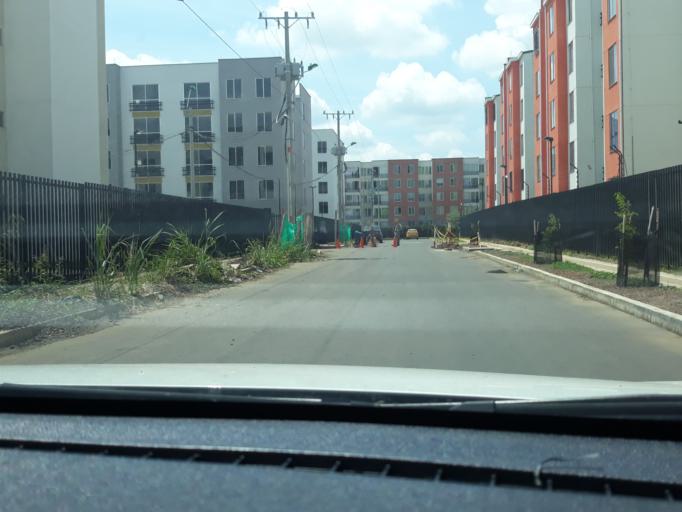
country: CO
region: Valle del Cauca
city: Cali
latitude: 3.3829
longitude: -76.5113
